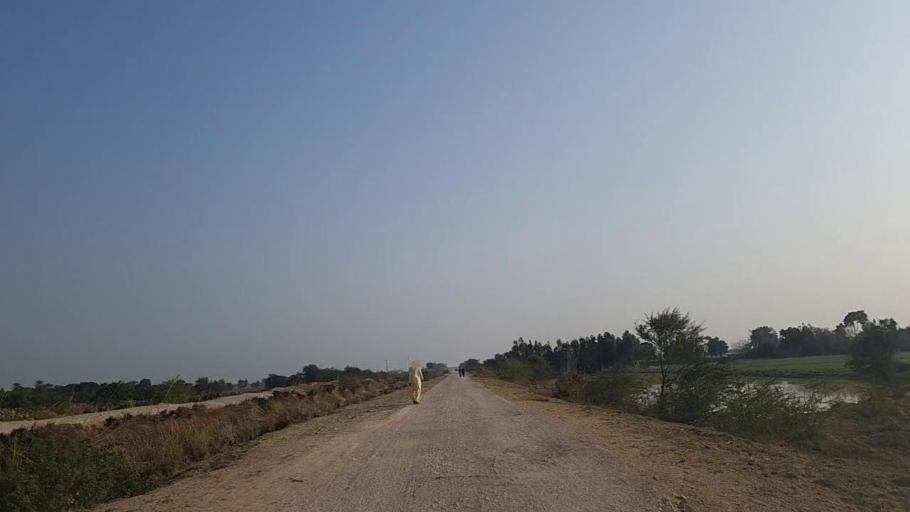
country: PK
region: Sindh
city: Jam Sahib
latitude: 26.2326
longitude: 68.5946
